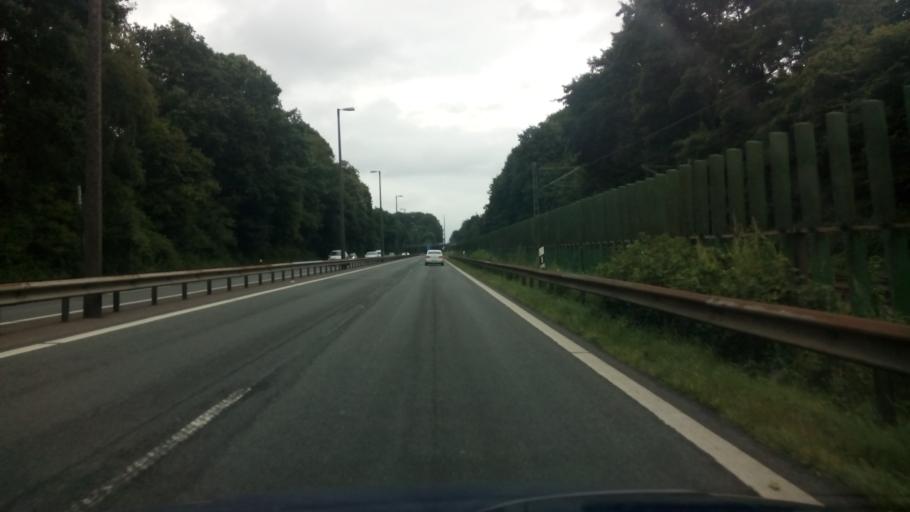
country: DE
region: Lower Saxony
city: Lemwerder
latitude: 53.1721
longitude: 8.6618
